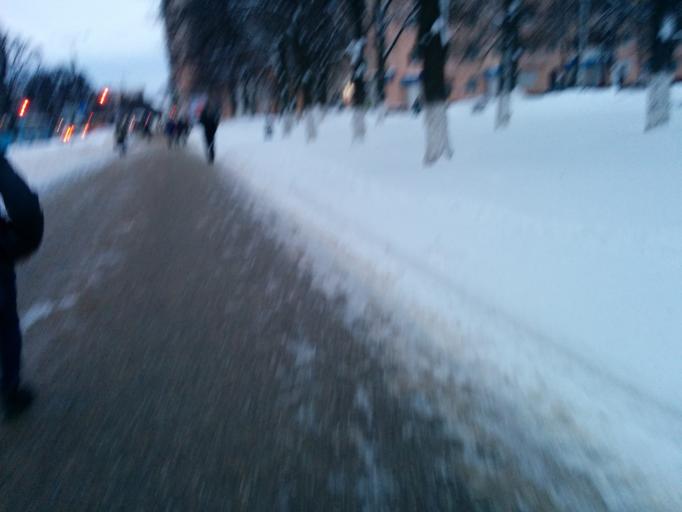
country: RU
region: Chuvashia
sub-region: Cheboksarskiy Rayon
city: Cheboksary
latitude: 56.1276
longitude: 47.2500
